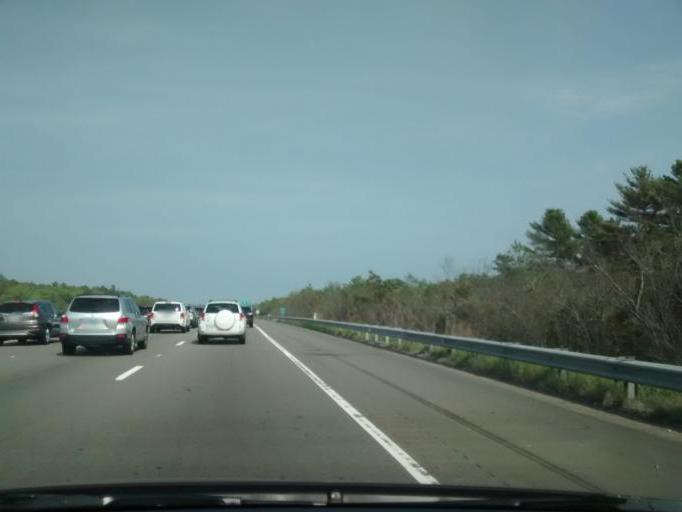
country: US
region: Massachusetts
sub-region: Plymouth County
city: White Island Shores
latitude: 41.7813
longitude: -70.6017
